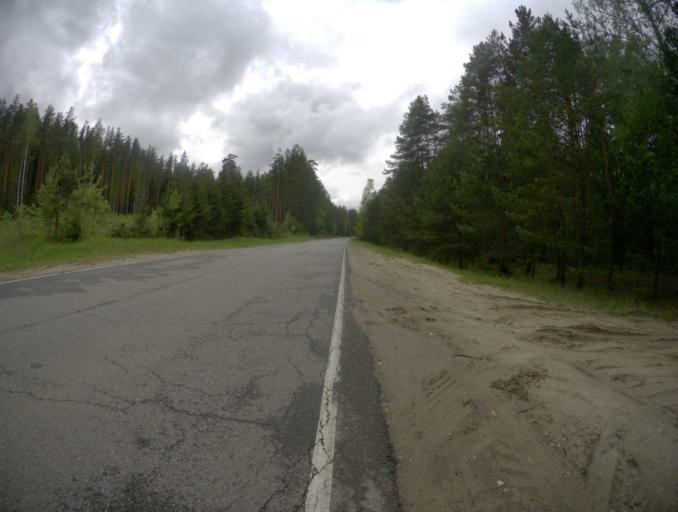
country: RU
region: Vladimir
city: Velikodvorskiy
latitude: 55.3946
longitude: 40.7170
